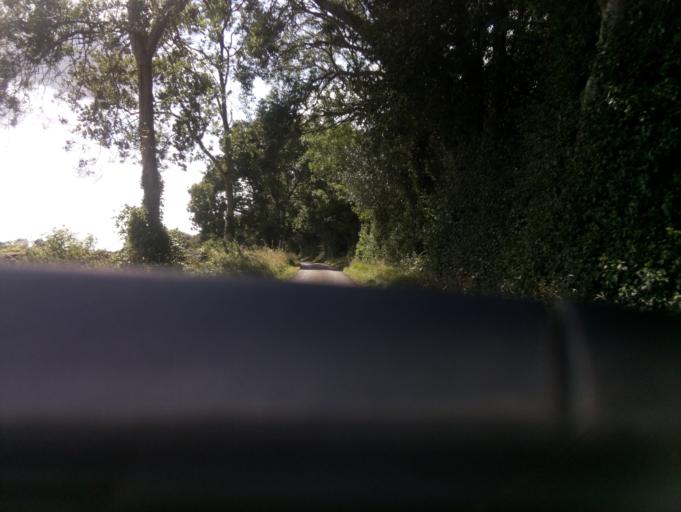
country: GB
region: England
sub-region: Gloucestershire
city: Coates
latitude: 51.6956
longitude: -2.0831
